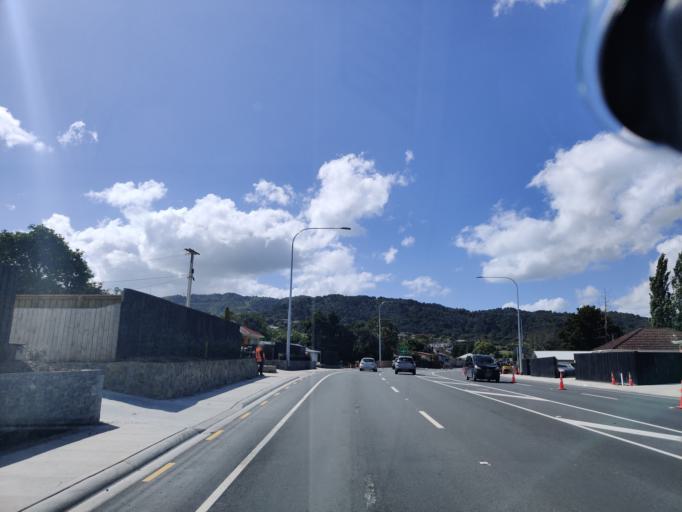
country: NZ
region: Northland
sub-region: Whangarei
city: Whangarei
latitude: -35.7345
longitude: 174.3102
